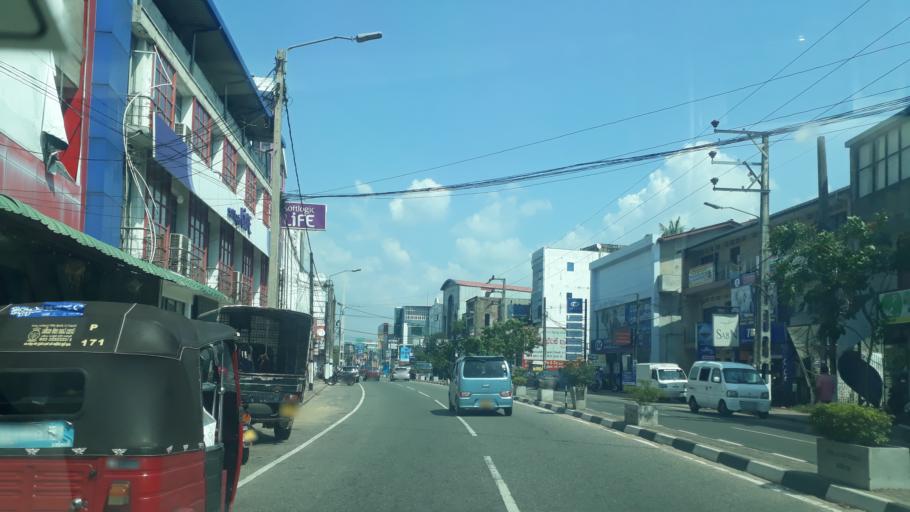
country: LK
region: Western
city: Gampaha
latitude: 7.0914
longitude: 79.9956
